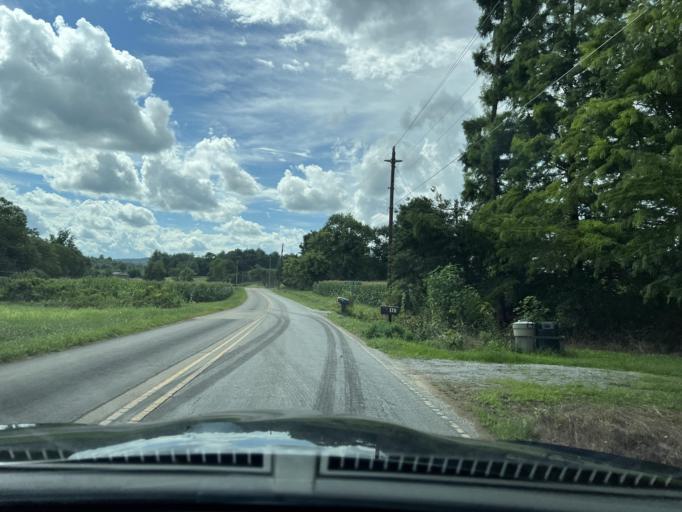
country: US
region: North Carolina
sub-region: Henderson County
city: Edneyville
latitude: 35.3914
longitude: -82.3650
